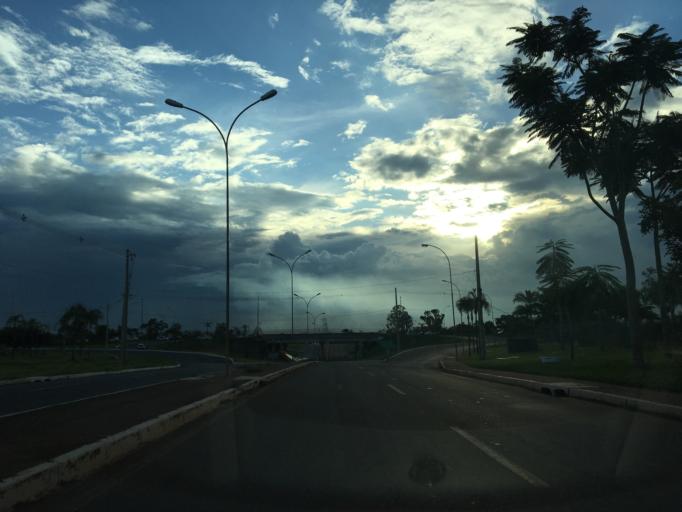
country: BR
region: Federal District
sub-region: Brasilia
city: Brasilia
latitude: -15.8105
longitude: -47.8436
